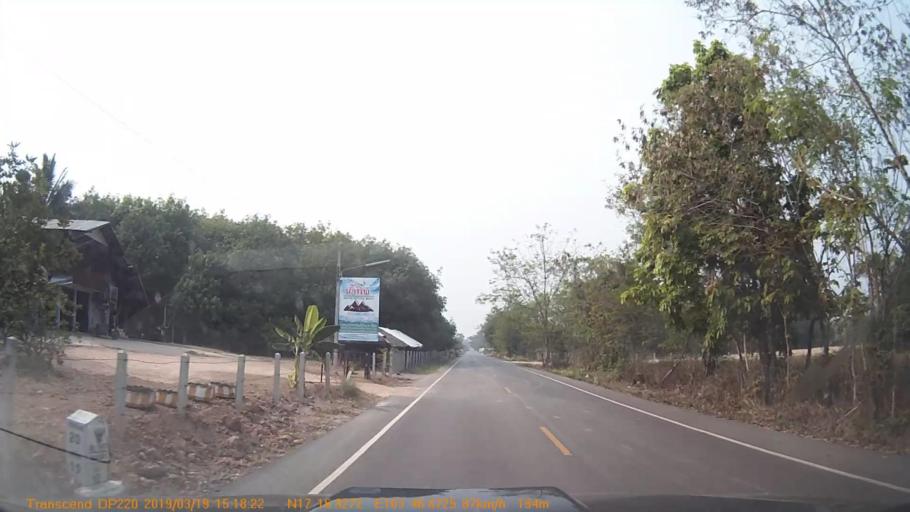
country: TH
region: Sakon Nakhon
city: Phanna Nikhom
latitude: 17.2826
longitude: 103.7776
